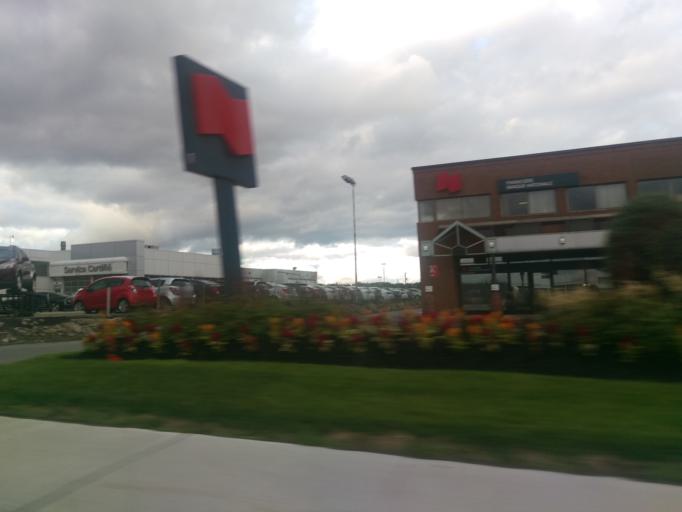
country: CA
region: Quebec
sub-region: Outaouais
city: Gatineau
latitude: 45.4661
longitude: -75.7387
